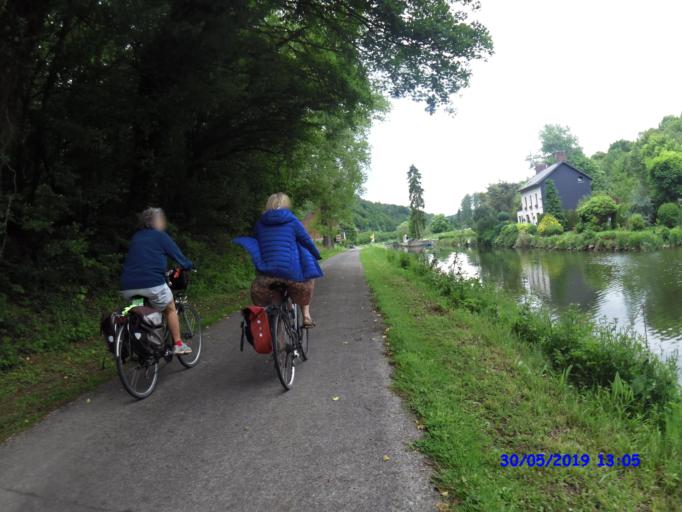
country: BE
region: Wallonia
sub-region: Province du Hainaut
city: Thuin
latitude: 50.3482
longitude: 4.3085
